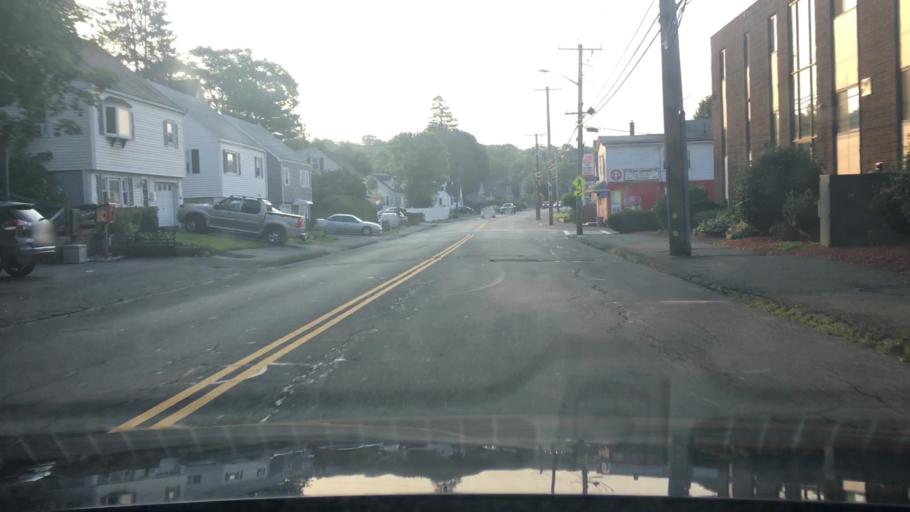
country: US
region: Massachusetts
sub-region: Essex County
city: Saugus
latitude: 42.4738
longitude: -70.9888
